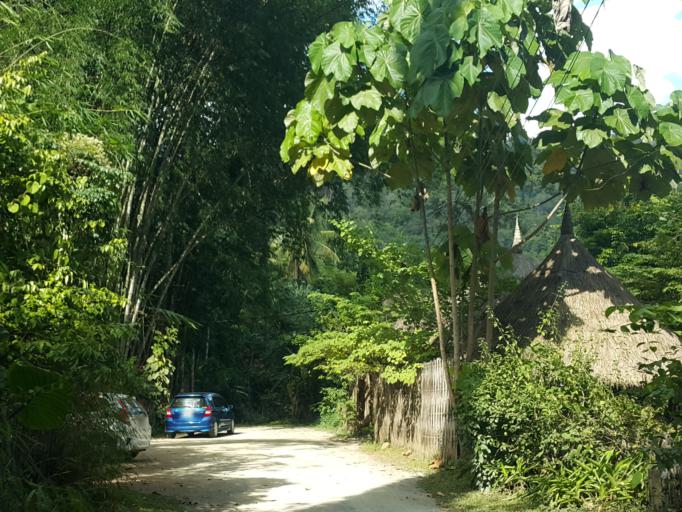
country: TH
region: Chiang Mai
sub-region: Amphoe Chiang Dao
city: Chiang Dao
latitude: 19.4042
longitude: 98.9258
